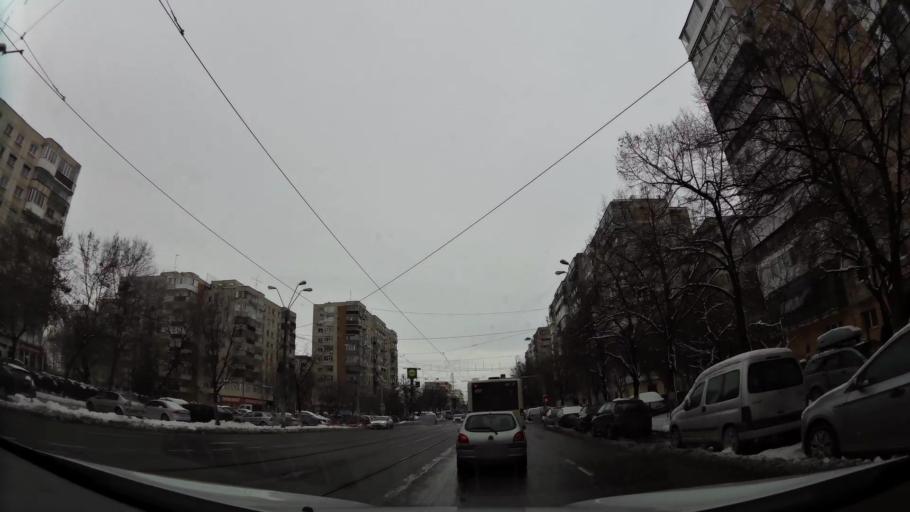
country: RO
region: Ilfov
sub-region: Comuna Popesti-Leordeni
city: Popesti-Leordeni
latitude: 44.3902
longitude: 26.1296
